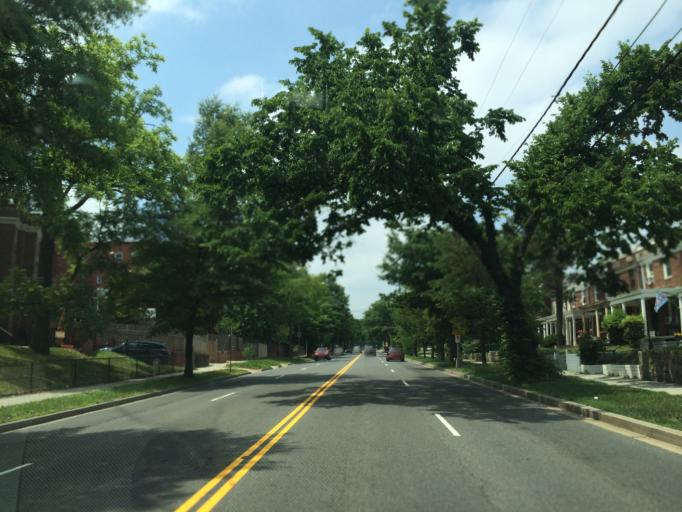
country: US
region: Maryland
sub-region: Montgomery County
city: Takoma Park
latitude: 38.9578
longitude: -77.0181
